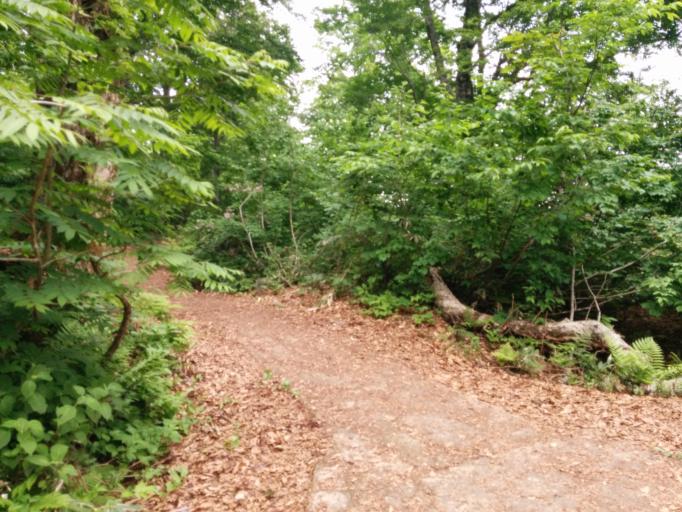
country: JP
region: Aomori
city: Hirosaki
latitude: 40.5547
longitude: 140.1649
